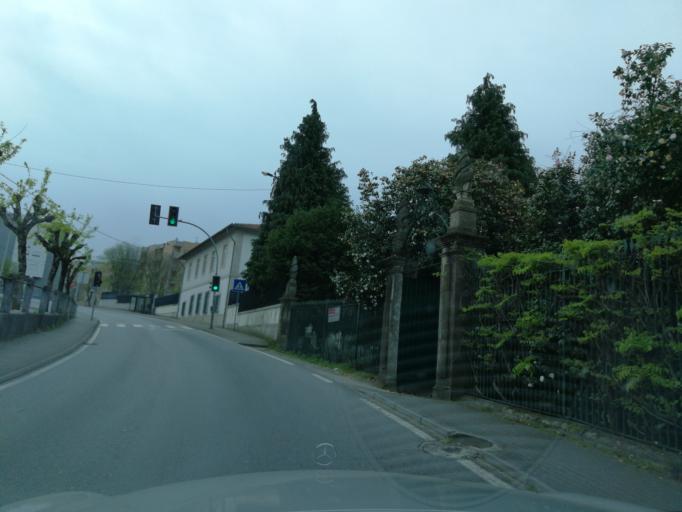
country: PT
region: Braga
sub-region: Braga
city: Braga
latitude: 41.5541
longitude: -8.4412
